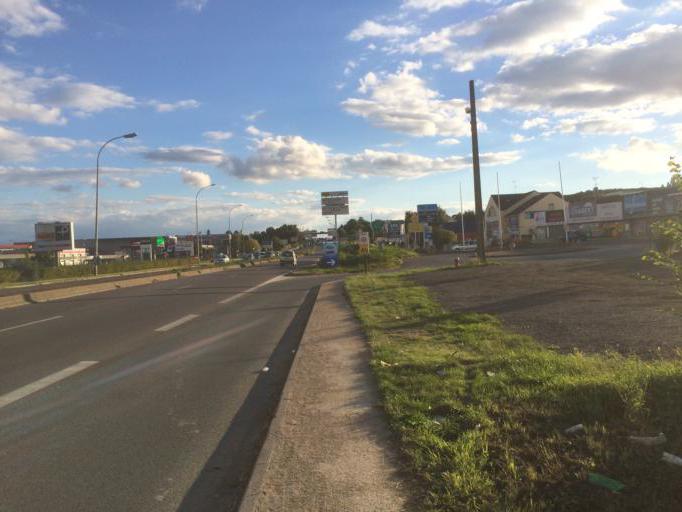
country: FR
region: Ile-de-France
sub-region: Departement de l'Essonne
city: La Ville-du-Bois
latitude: 48.6536
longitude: 2.2733
